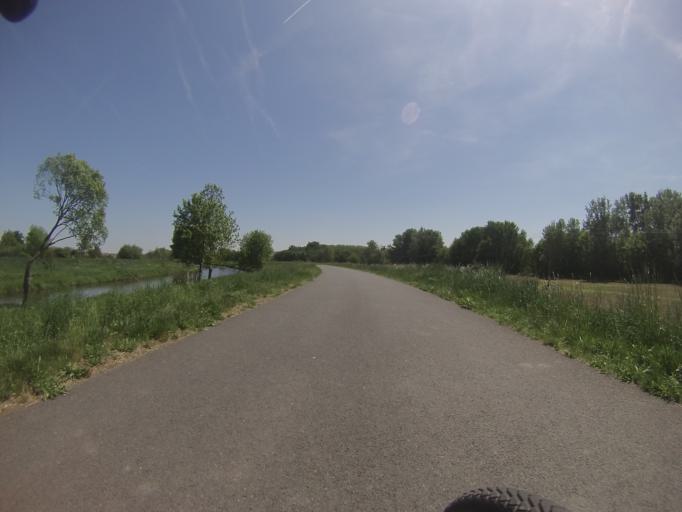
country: CZ
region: South Moravian
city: Vranovice
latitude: 48.9267
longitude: 16.5730
